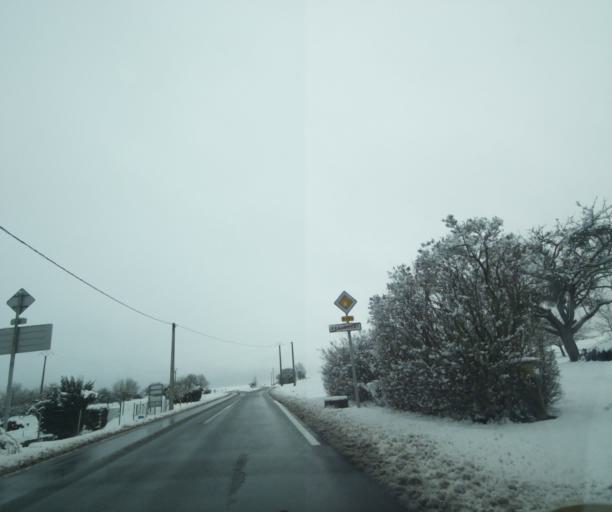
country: FR
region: Champagne-Ardenne
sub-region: Departement de la Haute-Marne
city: Montier-en-Der
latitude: 48.5315
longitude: 4.8163
